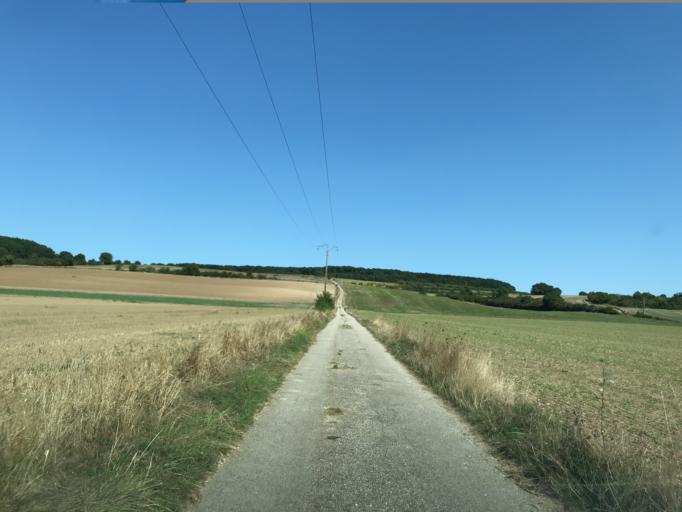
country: FR
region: Haute-Normandie
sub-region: Departement de l'Eure
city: Heudreville-sur-Eure
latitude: 49.1229
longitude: 1.2212
